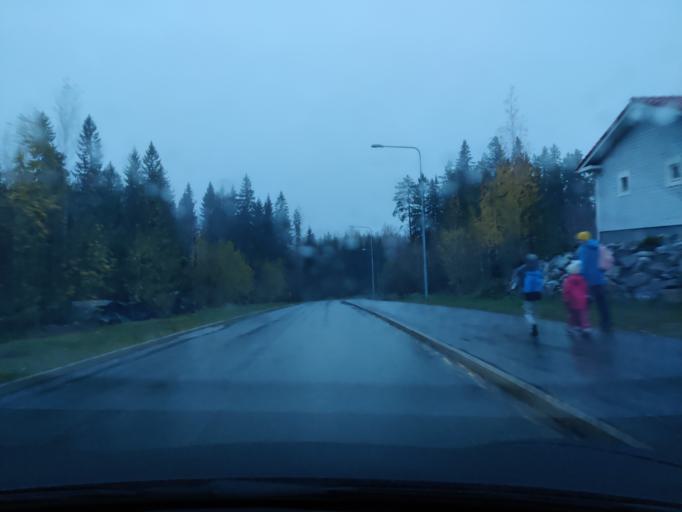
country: FI
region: Northern Savo
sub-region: Kuopio
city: Kuopio
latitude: 62.8293
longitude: 27.7169
